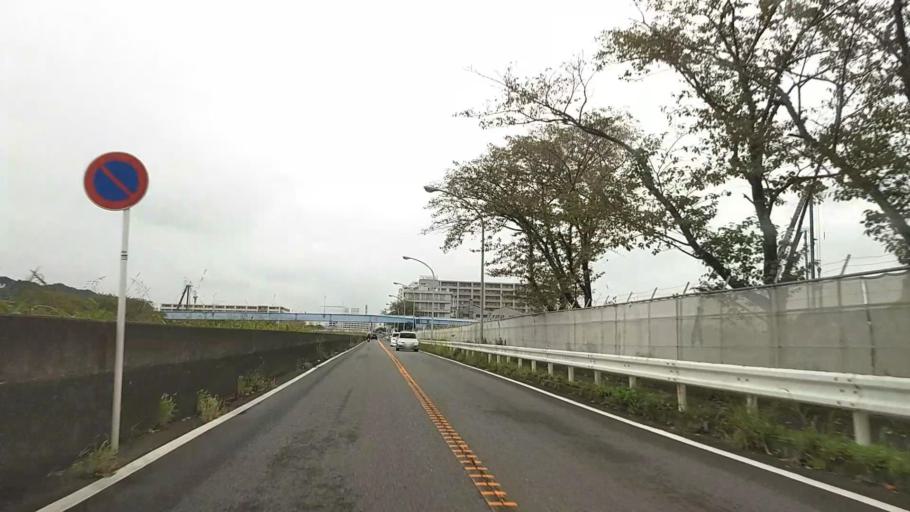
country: JP
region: Kanagawa
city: Fujisawa
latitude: 35.3911
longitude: 139.5332
